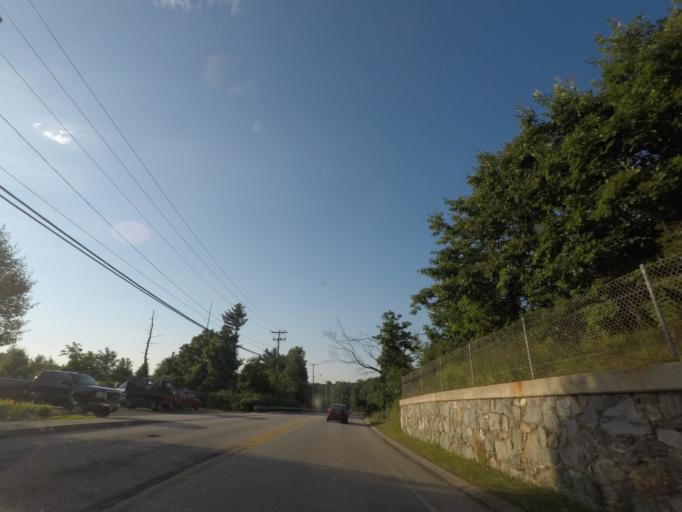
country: US
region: Massachusetts
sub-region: Worcester County
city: Sturbridge
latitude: 42.1023
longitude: -72.0758
